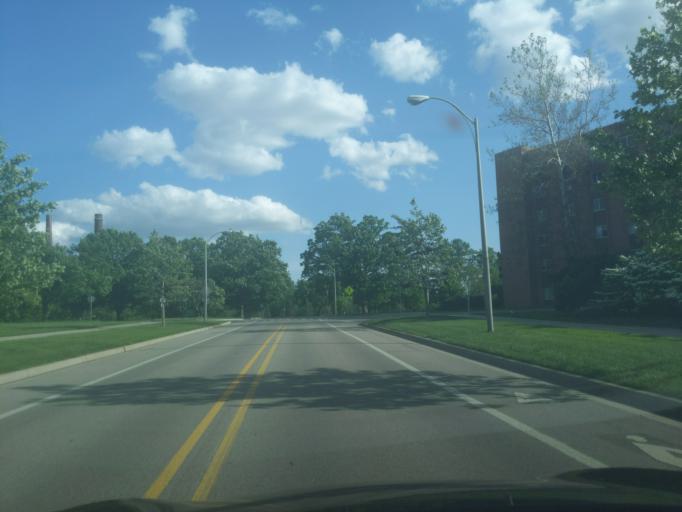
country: US
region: Michigan
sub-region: Ingham County
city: East Lansing
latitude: 42.7215
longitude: -84.4872
